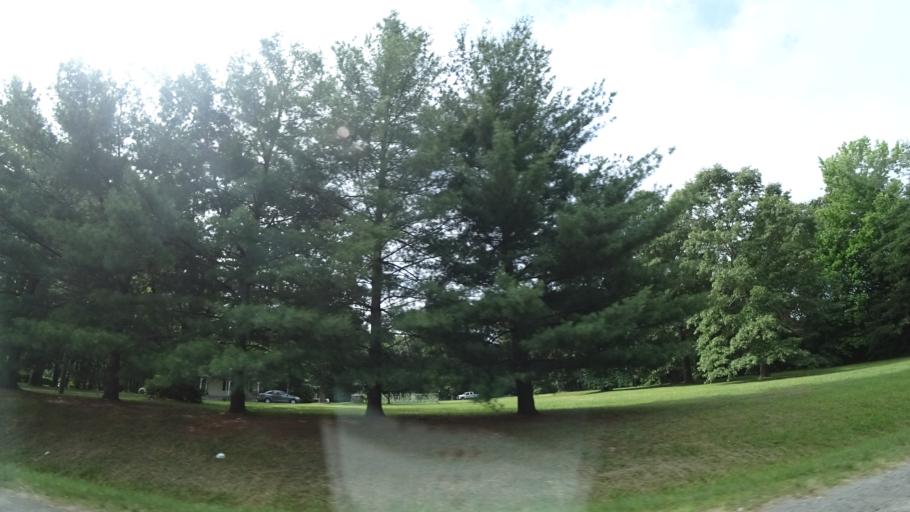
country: US
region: Virginia
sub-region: Spotsylvania County
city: Spotsylvania
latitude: 38.2392
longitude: -77.5421
